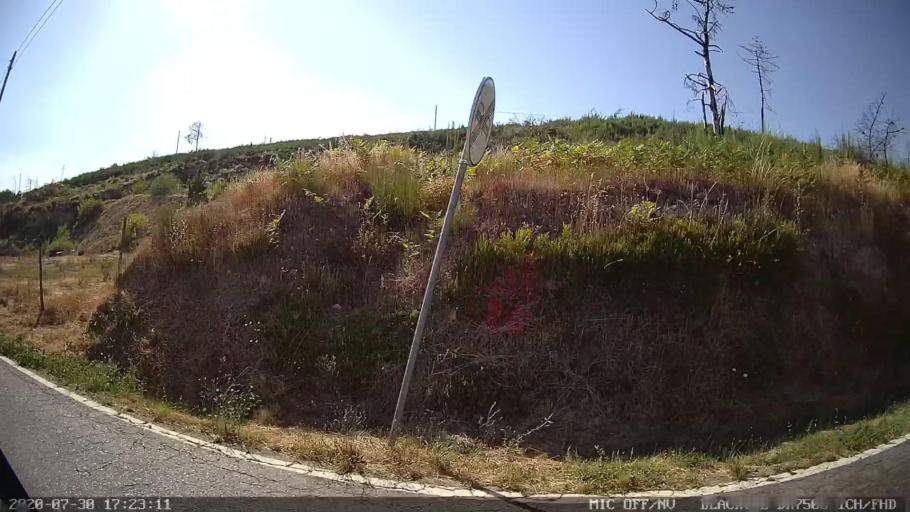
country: PT
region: Vila Real
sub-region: Murca
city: Murca
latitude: 41.3081
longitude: -7.4717
